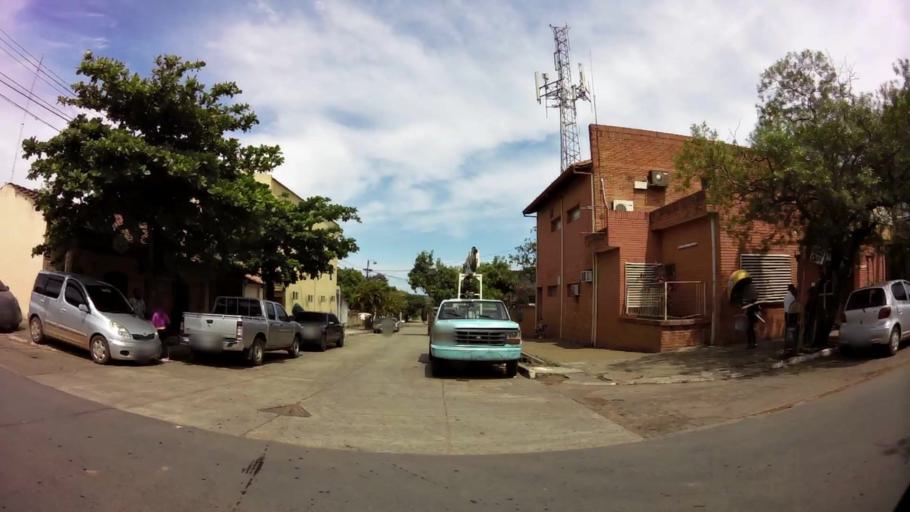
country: PY
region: Central
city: Limpio
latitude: -25.1657
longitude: -57.4749
